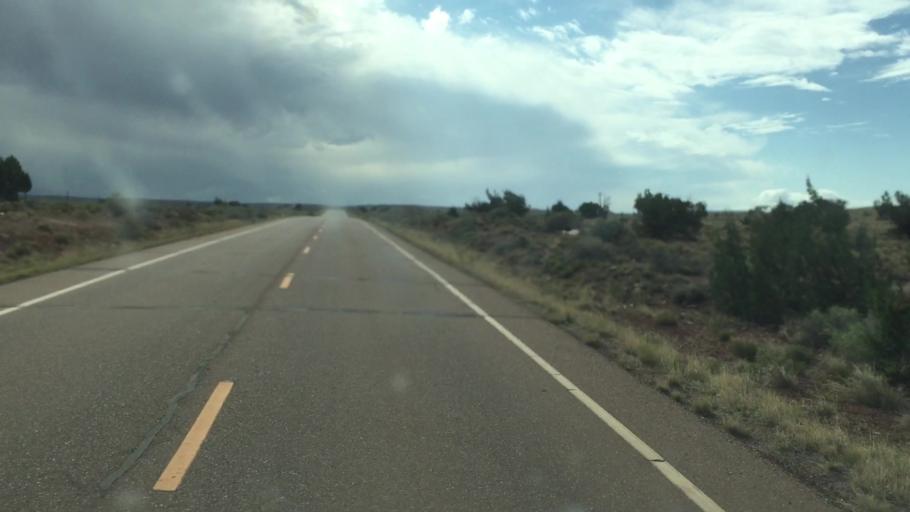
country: US
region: Arizona
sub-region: Apache County
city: Saint Johns
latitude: 34.5126
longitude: -109.6918
